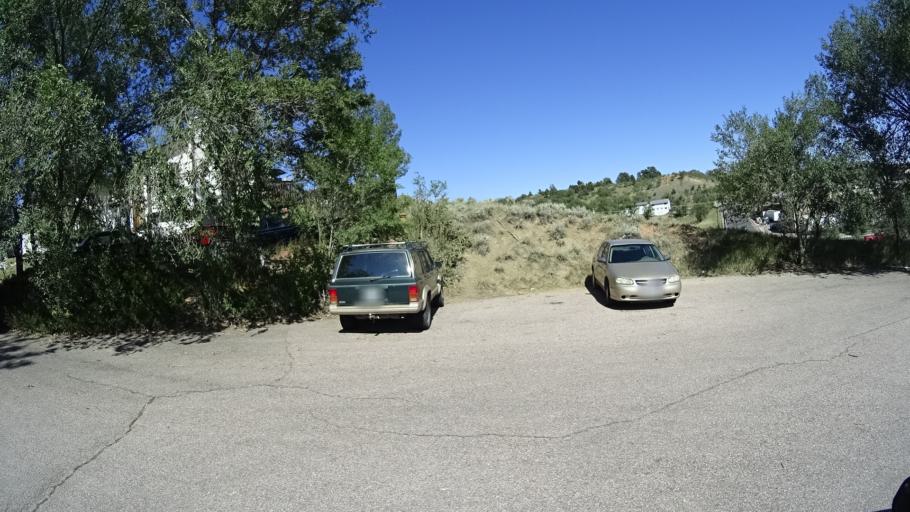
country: US
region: Colorado
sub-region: El Paso County
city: Colorado Springs
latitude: 38.8505
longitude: -104.8509
